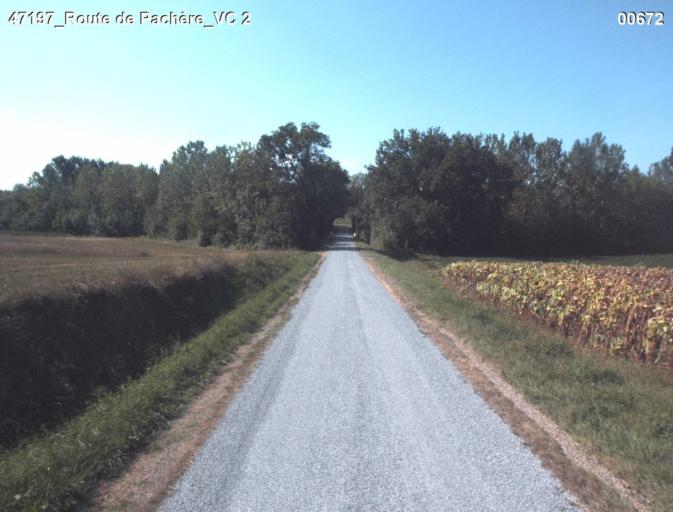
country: FR
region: Aquitaine
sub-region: Departement du Lot-et-Garonne
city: Laplume
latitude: 44.0904
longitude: 0.4642
